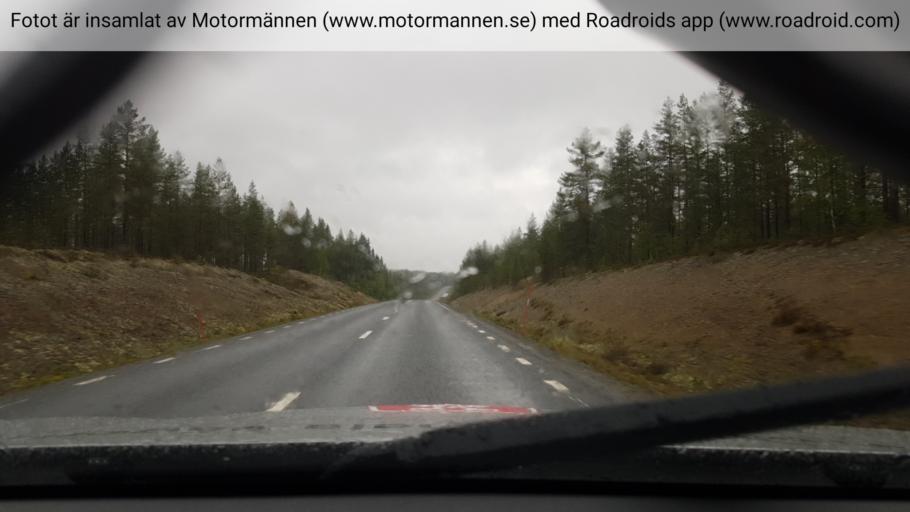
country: SE
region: Vaesterbotten
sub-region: Bjurholms Kommun
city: Bjurholm
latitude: 63.9865
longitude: 18.8037
